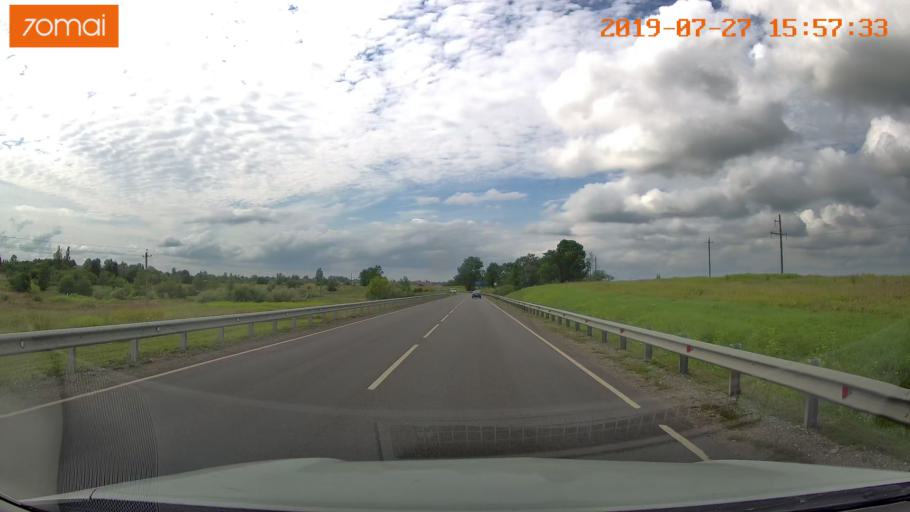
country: RU
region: Kaliningrad
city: Chernyakhovsk
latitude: 54.6240
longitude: 21.8822
